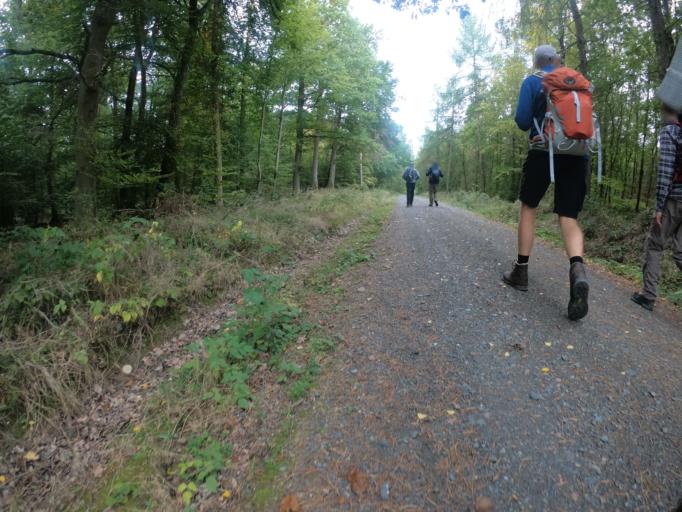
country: DE
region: Hesse
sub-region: Regierungsbezirk Darmstadt
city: Waldems
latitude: 50.2154
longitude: 8.3113
